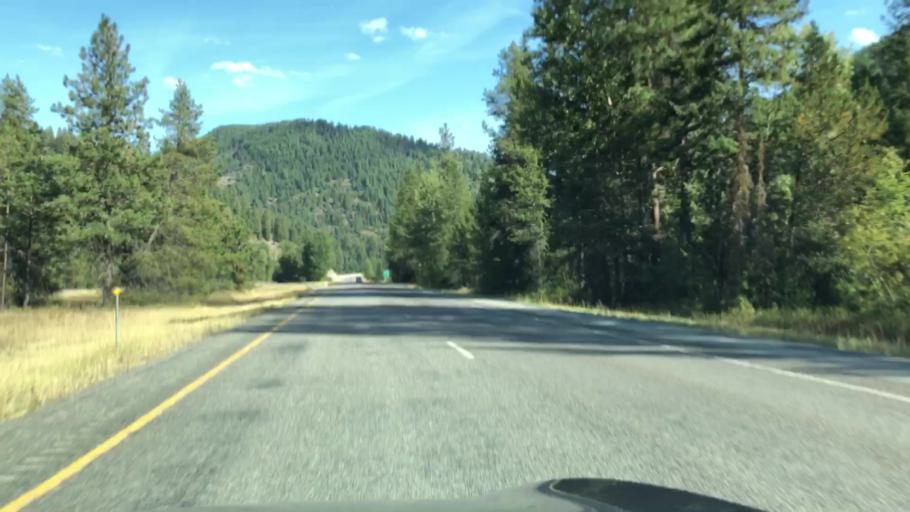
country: US
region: Montana
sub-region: Sanders County
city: Thompson Falls
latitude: 47.3578
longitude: -115.3065
